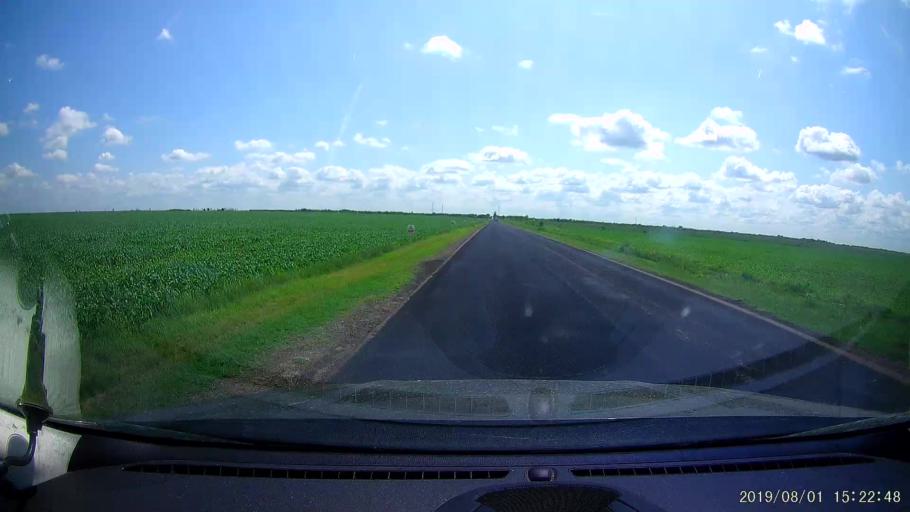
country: RO
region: Braila
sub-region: Comuna Viziru
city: Lanurile
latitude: 45.0492
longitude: 27.7708
